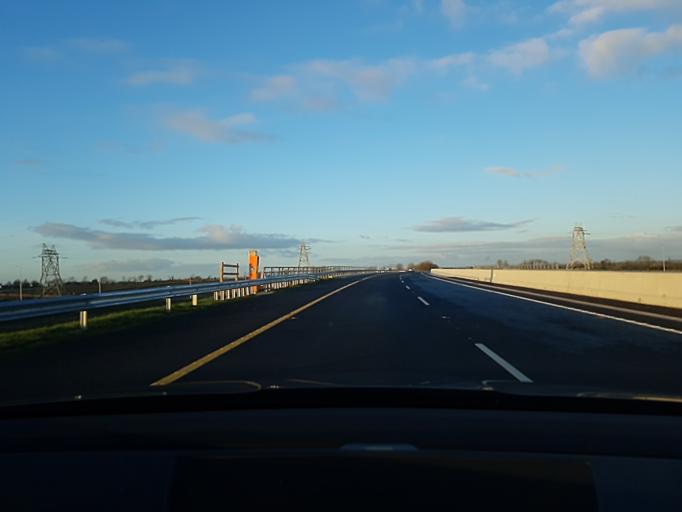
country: IE
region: Connaught
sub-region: County Galway
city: Athenry
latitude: 53.2964
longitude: -8.8077
